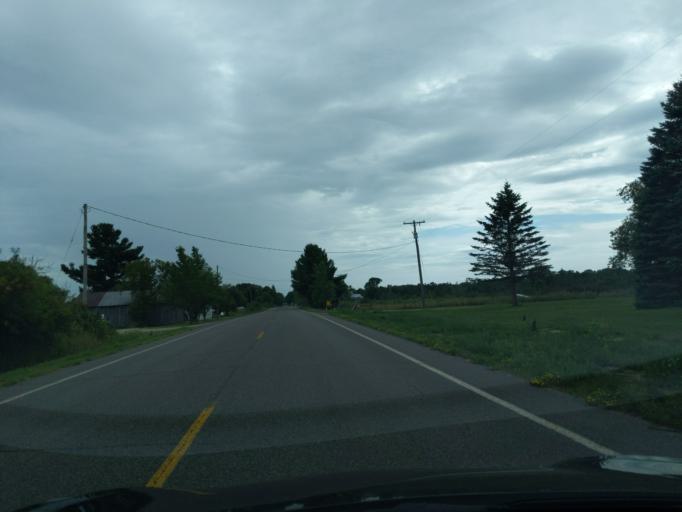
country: US
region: Michigan
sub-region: Clare County
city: Harrison
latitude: 44.0095
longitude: -84.9492
